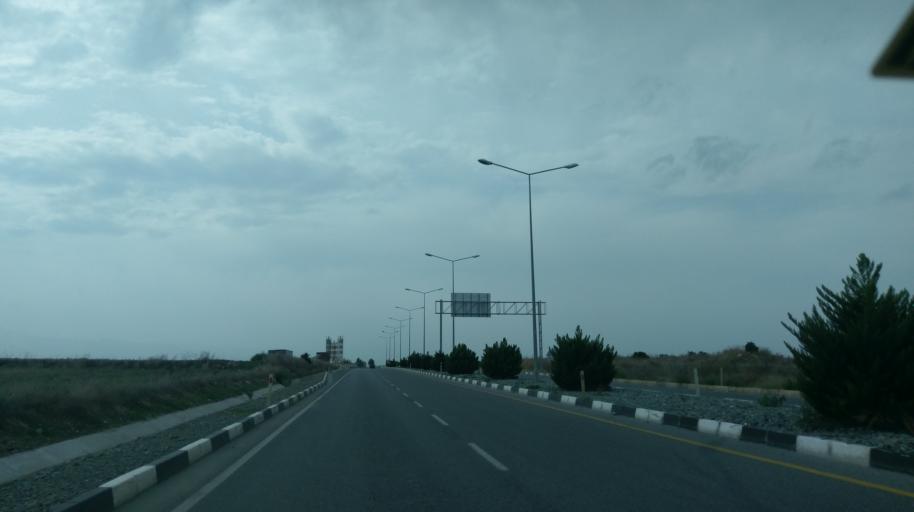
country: CY
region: Lefkosia
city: Morfou
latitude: 35.2048
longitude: 33.0424
